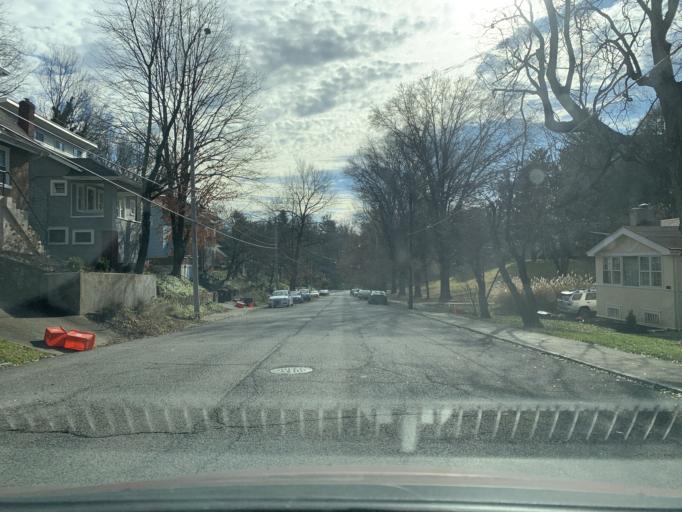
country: US
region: Kentucky
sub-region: Jefferson County
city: Indian Hills
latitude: 38.2505
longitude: -85.6952
